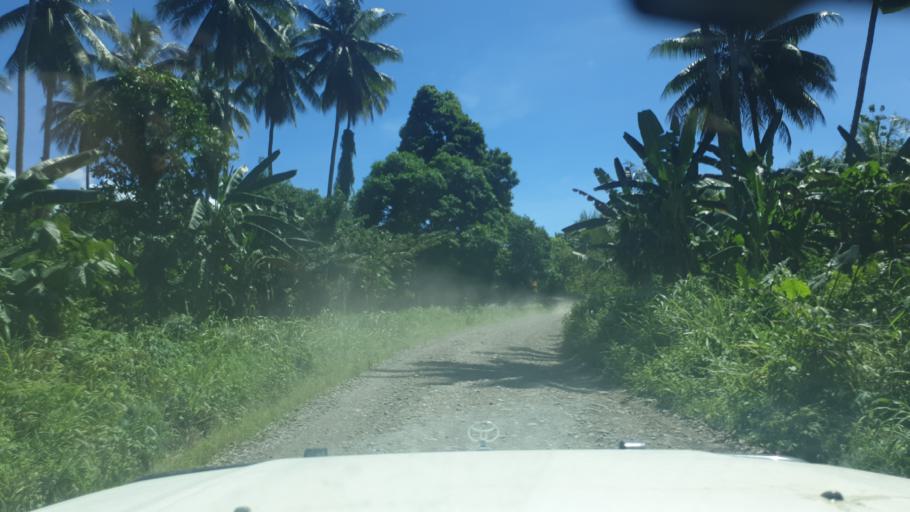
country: PG
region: Bougainville
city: Buka
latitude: -5.6686
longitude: 155.1016
